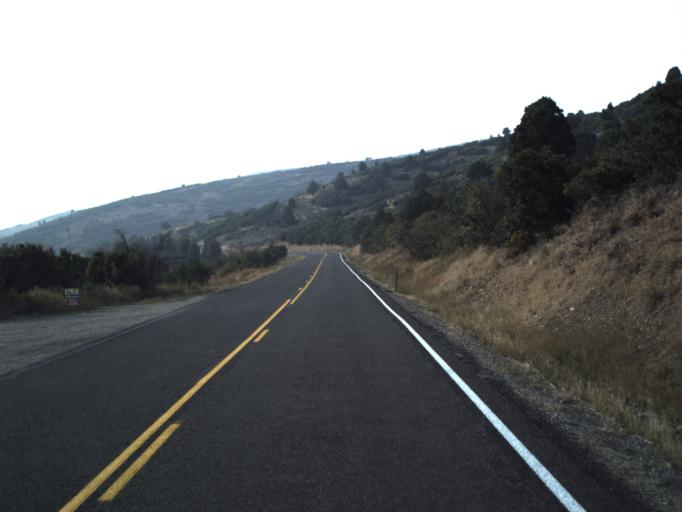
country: US
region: Utah
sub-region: Summit County
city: Francis
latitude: 40.6227
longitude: -111.2238
